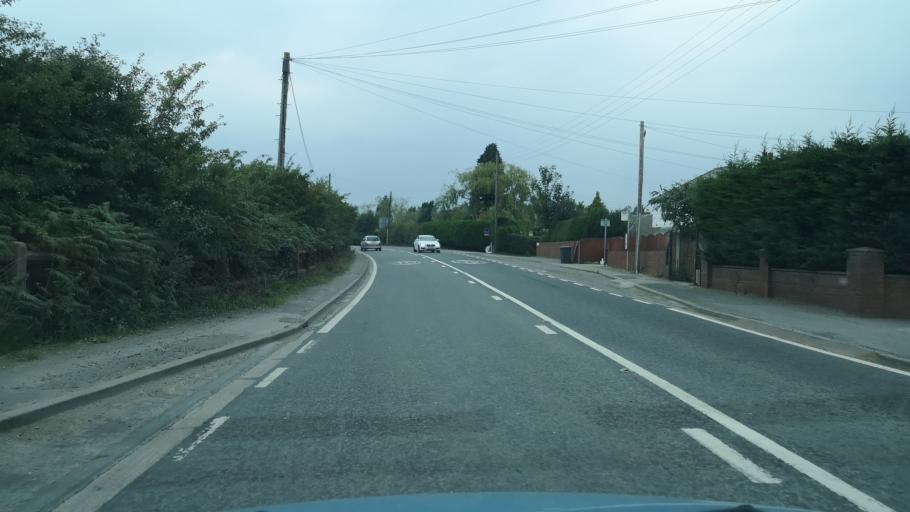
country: GB
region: England
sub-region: East Riding of Yorkshire
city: Pollington
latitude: 53.6991
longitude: -1.1237
